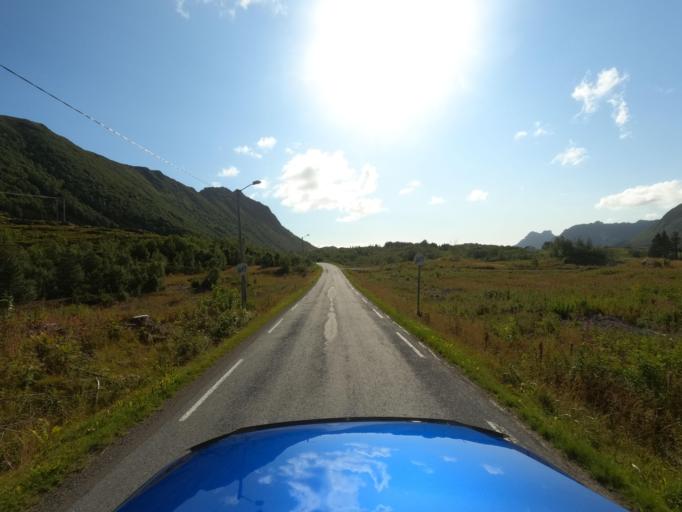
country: NO
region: Nordland
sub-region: Vestvagoy
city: Evjen
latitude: 68.1437
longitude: 13.7716
